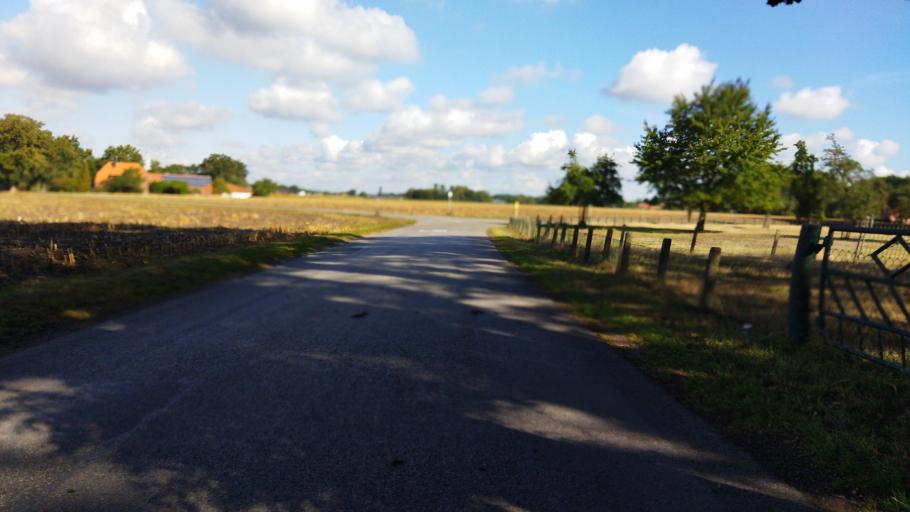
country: DE
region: Lower Saxony
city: Salzbergen
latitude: 52.3096
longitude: 7.3246
